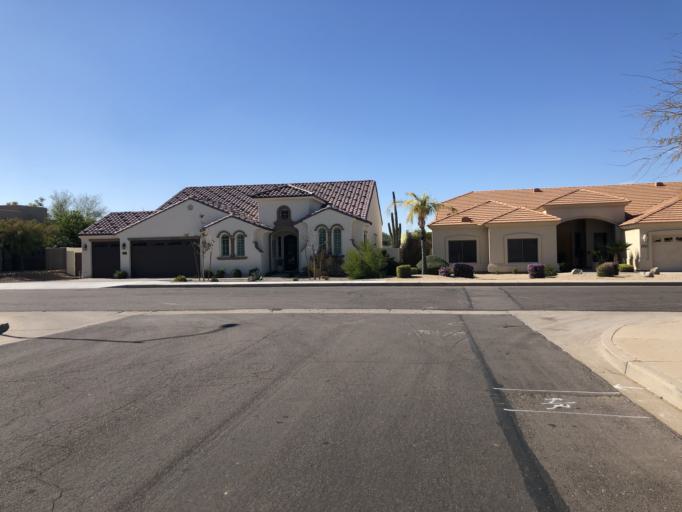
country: US
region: Arizona
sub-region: Maricopa County
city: Mesa
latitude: 33.4692
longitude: -111.6962
